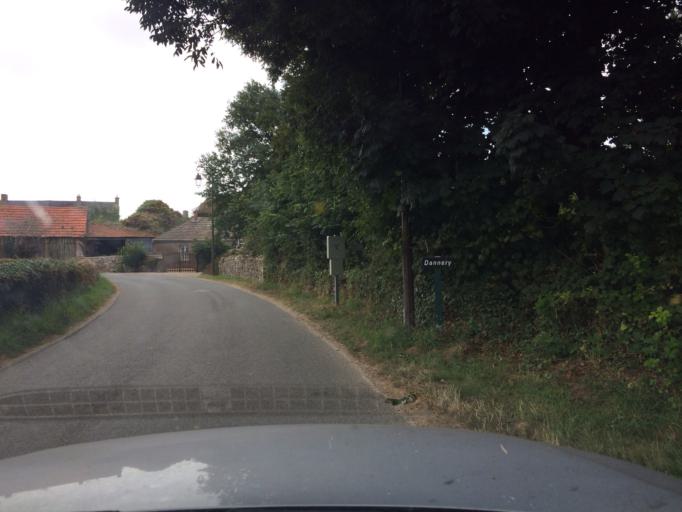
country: FR
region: Lower Normandy
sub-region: Departement de la Manche
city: Beaumont-Hague
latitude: 49.6770
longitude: -1.9186
